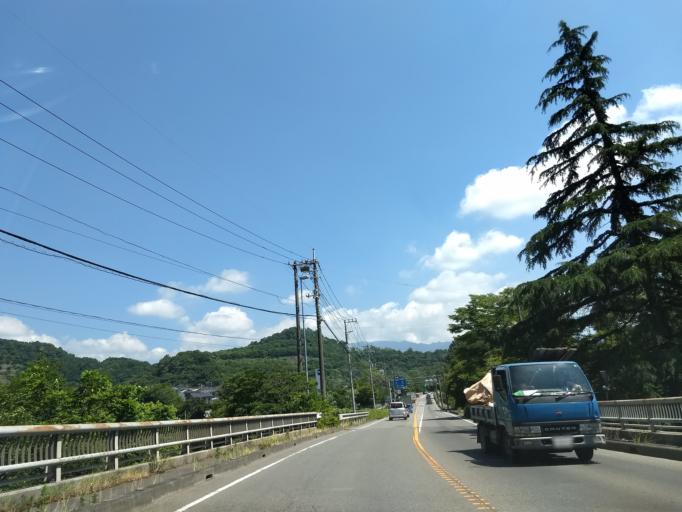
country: JP
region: Kanagawa
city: Hadano
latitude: 35.3611
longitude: 139.1581
